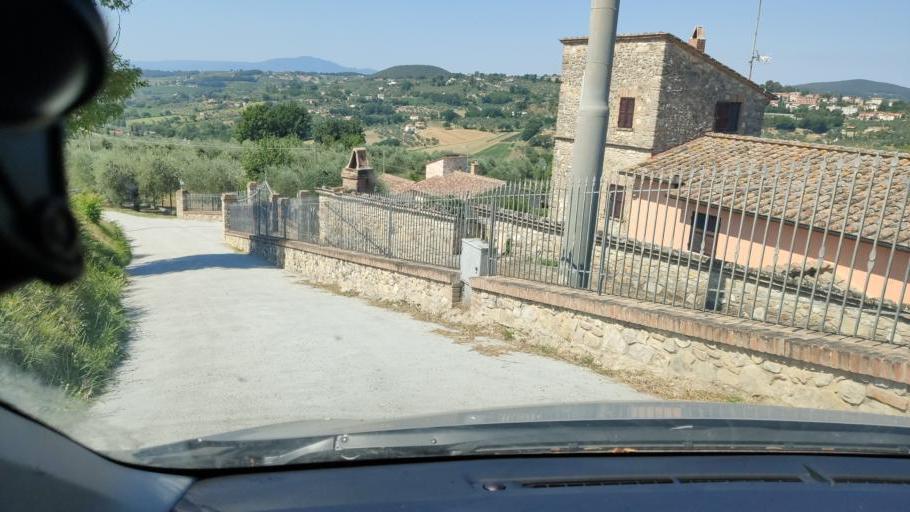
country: IT
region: Umbria
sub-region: Provincia di Terni
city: Amelia
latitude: 42.5461
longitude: 12.4343
